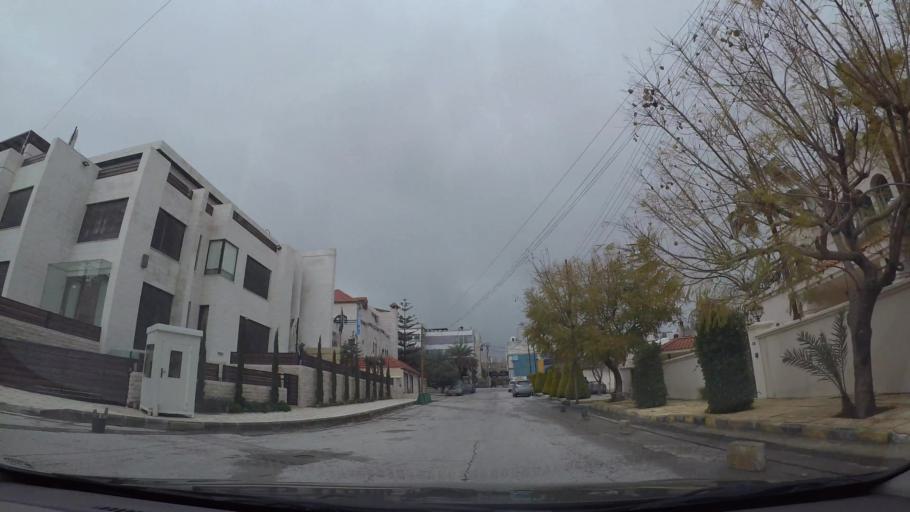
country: JO
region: Amman
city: Al Bunayyat ash Shamaliyah
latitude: 31.9400
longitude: 35.8857
